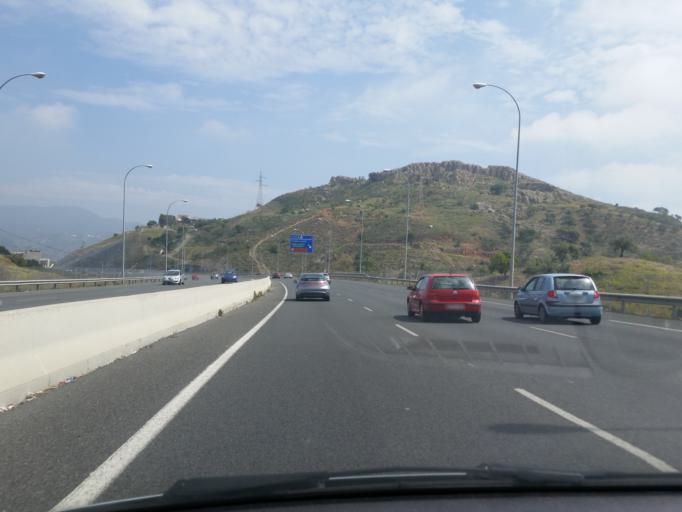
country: ES
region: Andalusia
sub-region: Provincia de Malaga
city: Malaga
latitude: 36.7404
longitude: -4.4491
